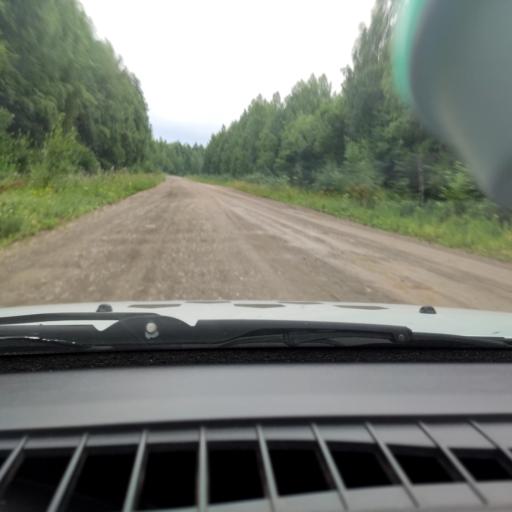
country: RU
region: Perm
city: Dobryanka
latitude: 58.6217
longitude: 56.7103
